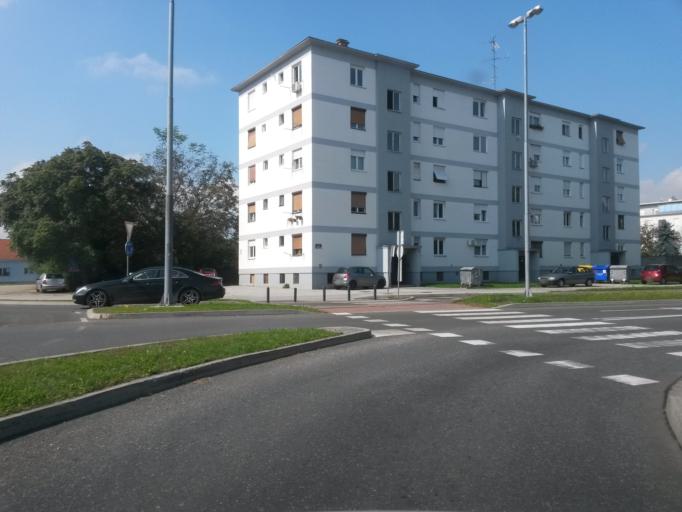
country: HR
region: Varazdinska
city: Varazdin
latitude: 46.2982
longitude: 16.3371
